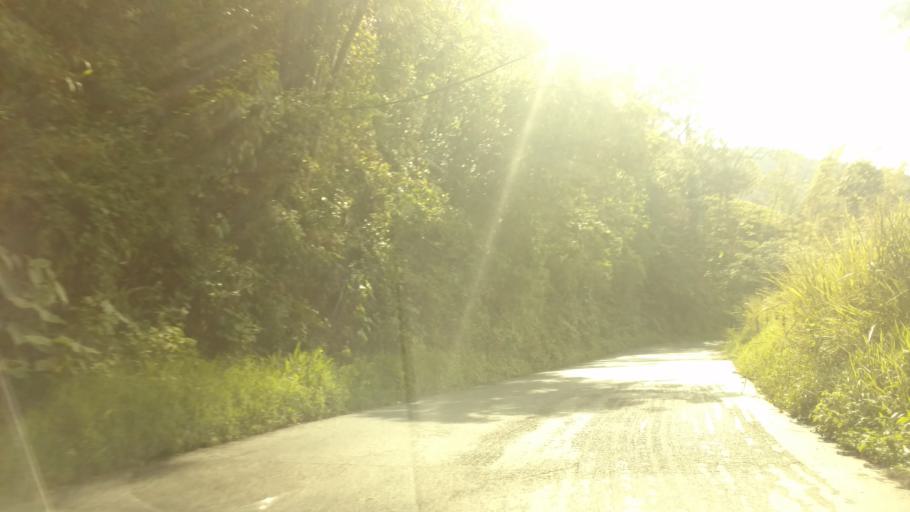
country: CO
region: Caldas
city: Neira
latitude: 5.1799
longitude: -75.5225
